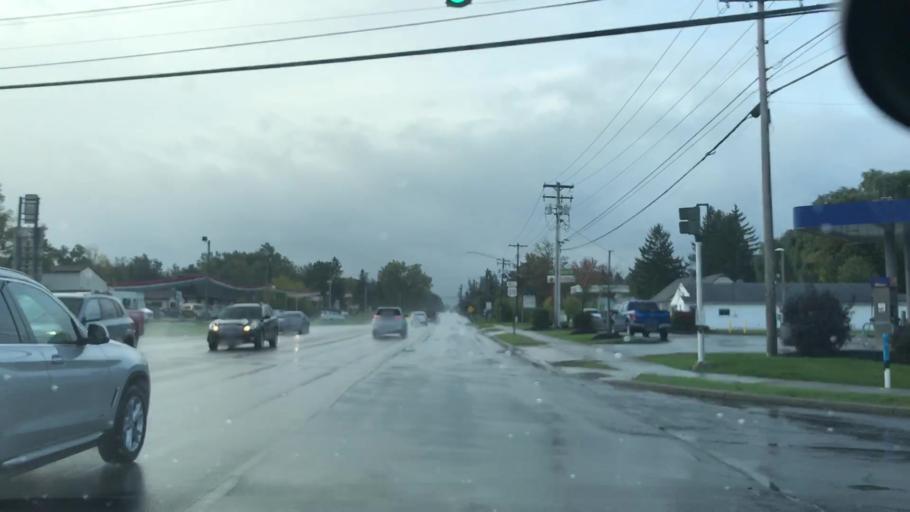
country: US
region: New York
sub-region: Erie County
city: Elma Center
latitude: 42.8274
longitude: -78.6970
